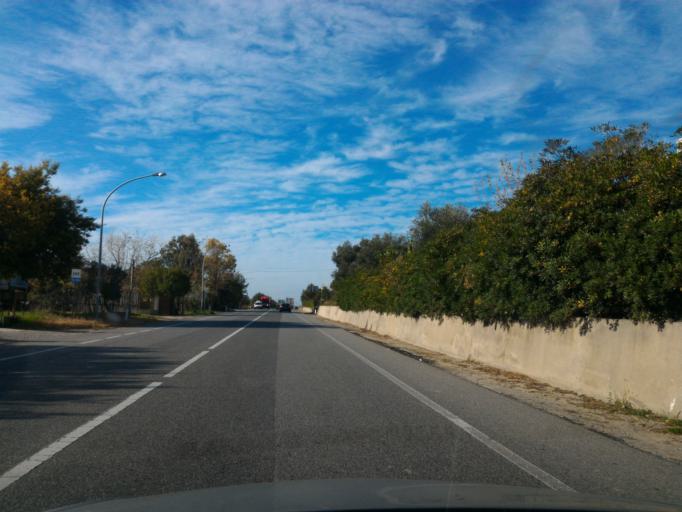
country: IT
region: Calabria
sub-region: Provincia di Catanzaro
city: Cropani Marina
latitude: 38.9273
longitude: 16.8250
